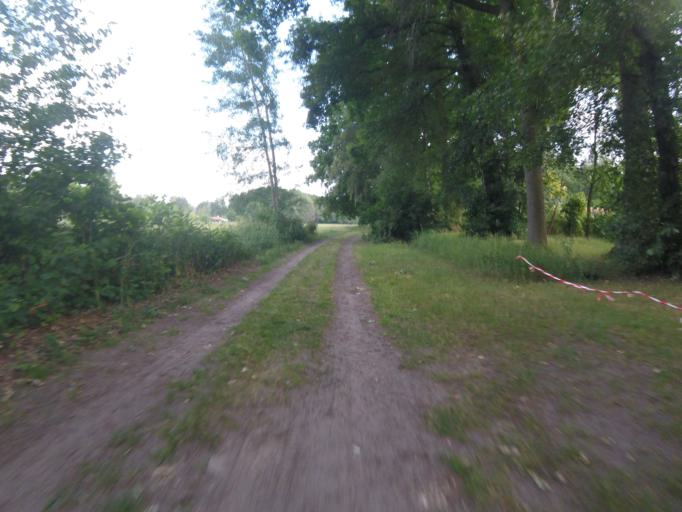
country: DE
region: Brandenburg
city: Bestensee
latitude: 52.2703
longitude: 13.6365
